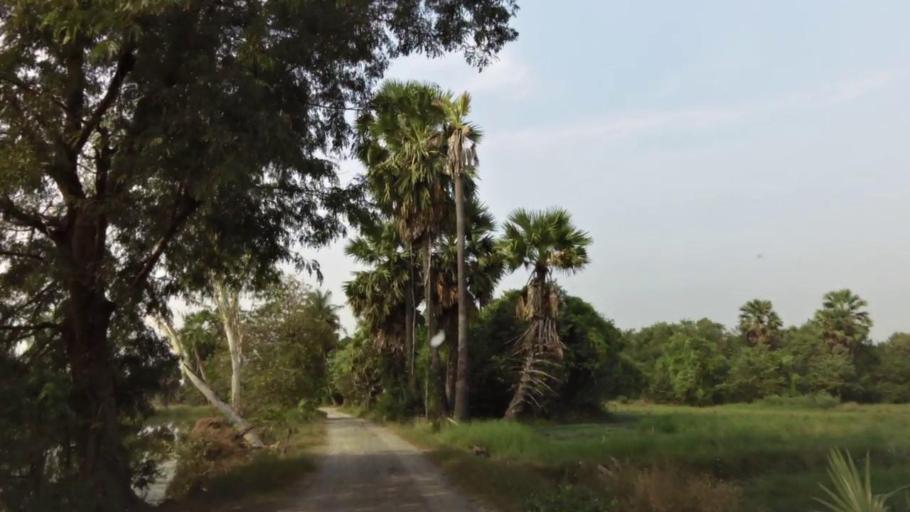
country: TH
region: Phra Nakhon Si Ayutthaya
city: Phra Nakhon Si Ayutthaya
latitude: 14.3409
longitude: 100.5690
